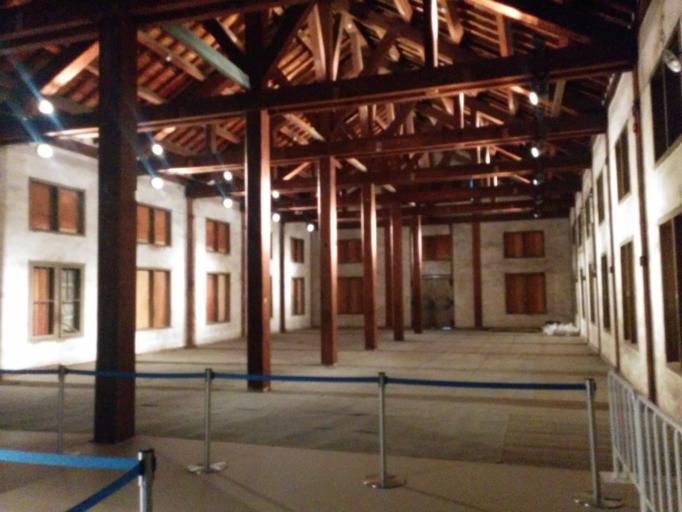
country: JP
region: Gunma
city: Tomioka
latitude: 36.2556
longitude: 138.8881
